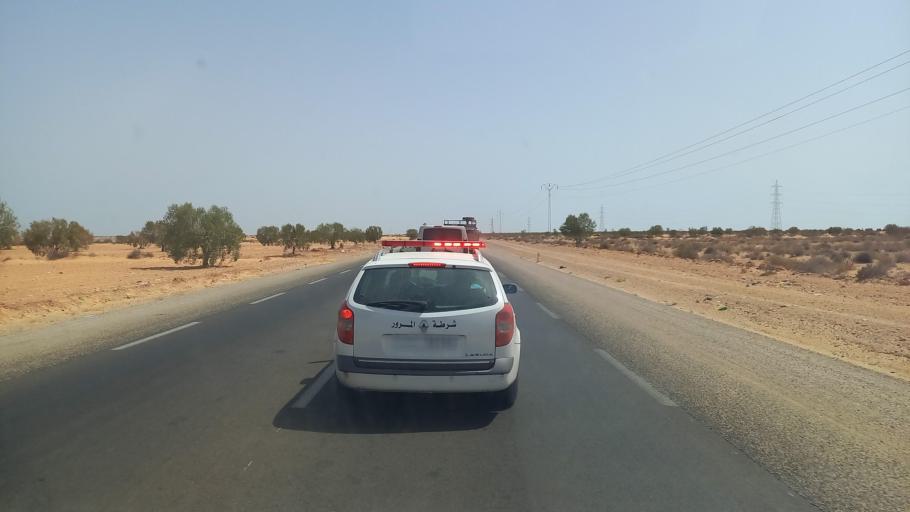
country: TN
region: Madanin
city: Zarzis
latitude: 33.4002
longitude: 10.8367
